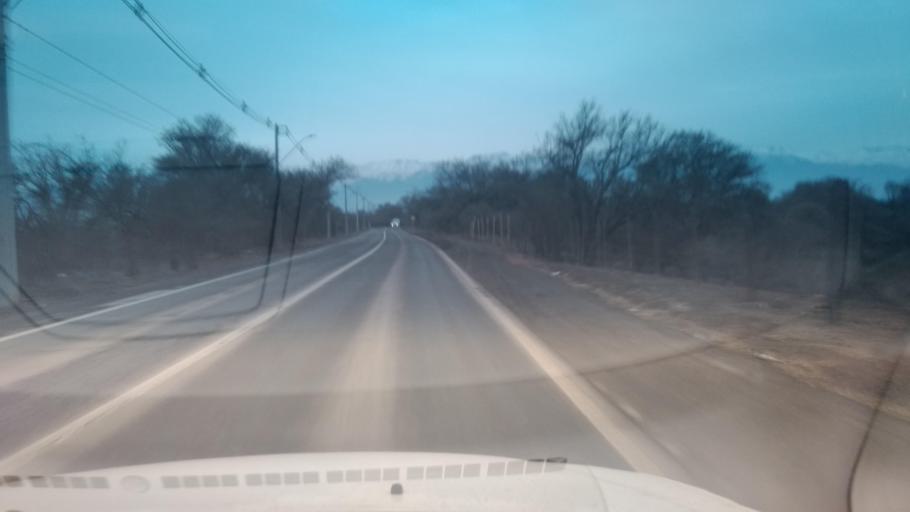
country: CL
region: Santiago Metropolitan
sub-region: Provincia de Chacabuco
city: Chicureo Abajo
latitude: -33.0919
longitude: -70.7388
